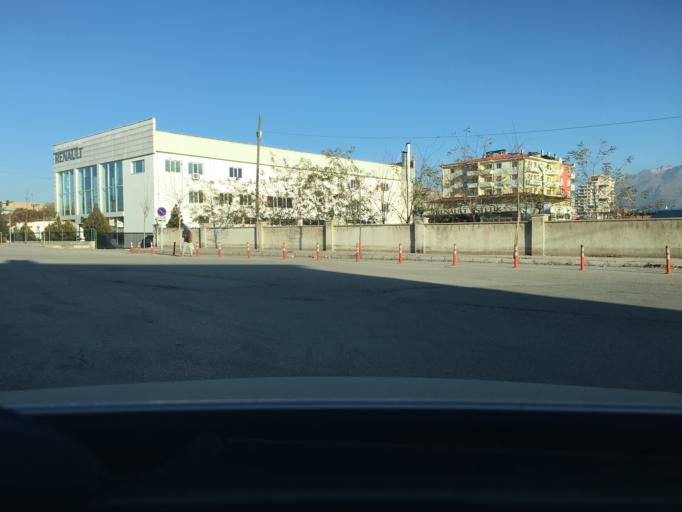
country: TR
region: Van
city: Van
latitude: 38.5221
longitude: 43.3594
